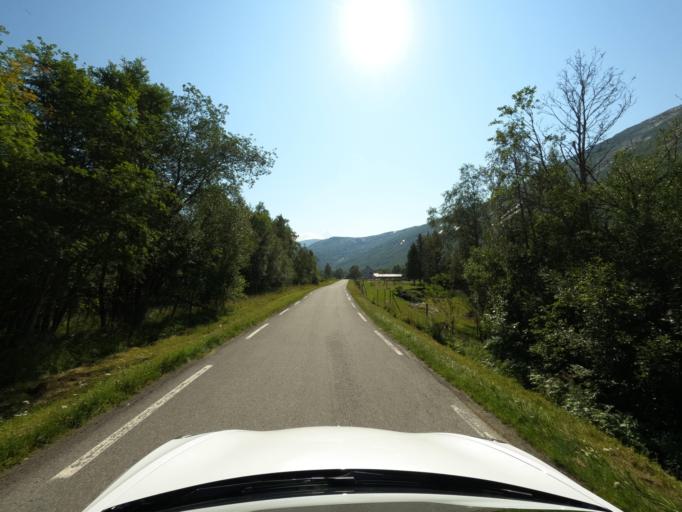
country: NO
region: Nordland
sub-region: Narvik
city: Narvik
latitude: 68.1839
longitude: 17.5561
